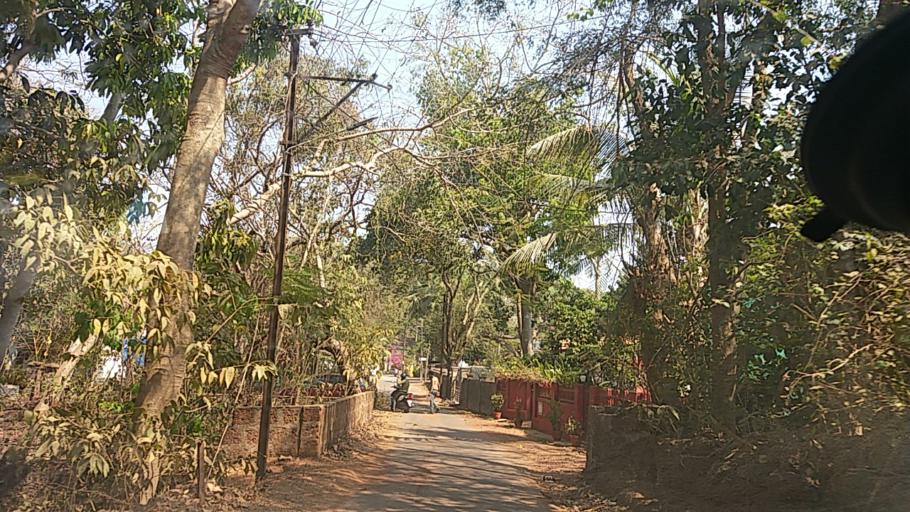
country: IN
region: Goa
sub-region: North Goa
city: Saligao
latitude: 15.5378
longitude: 73.7859
